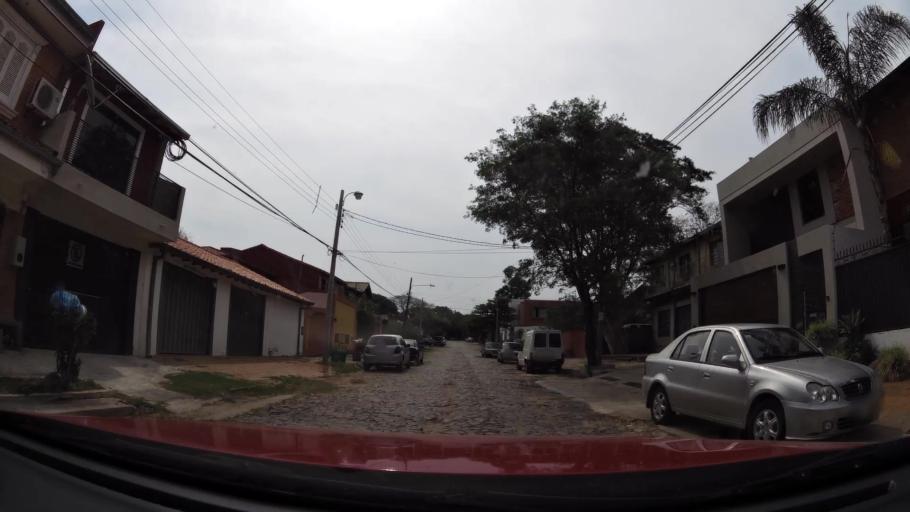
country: PY
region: Central
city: Fernando de la Mora
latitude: -25.2723
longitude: -57.5576
